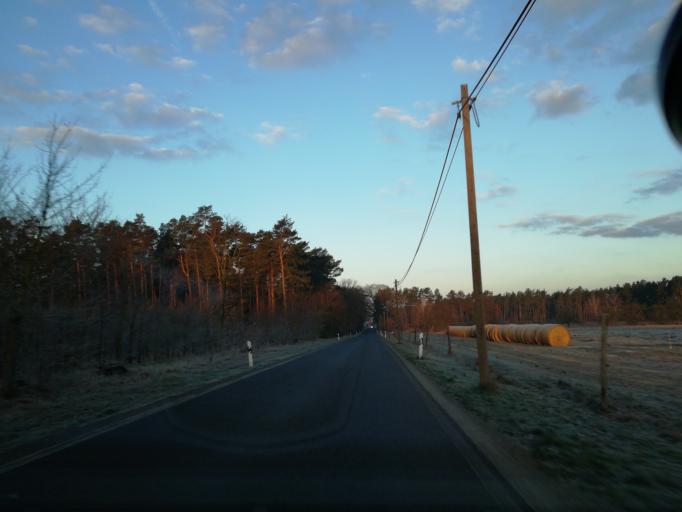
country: DE
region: Brandenburg
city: Crinitz
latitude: 51.7219
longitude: 13.8498
